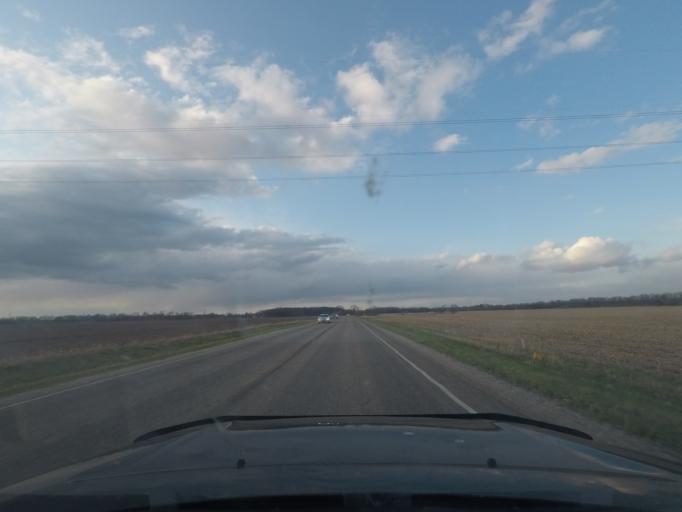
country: US
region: Indiana
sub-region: LaPorte County
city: Kingsford Heights
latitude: 41.5345
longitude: -86.7406
